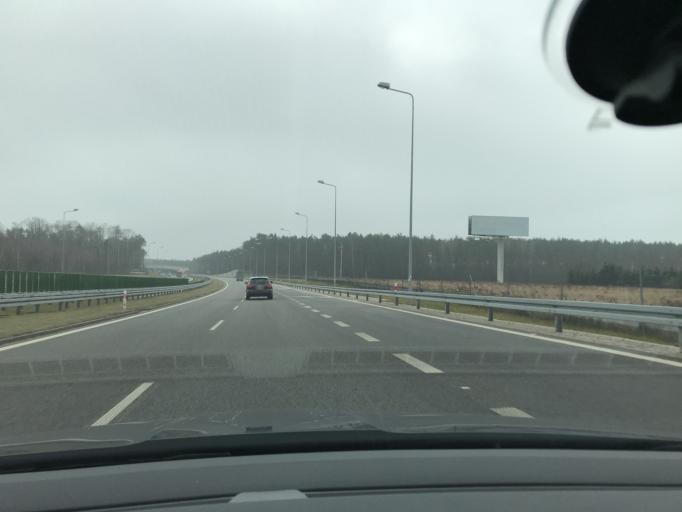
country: PL
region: Lodz Voivodeship
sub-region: Powiat pabianicki
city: Dobron
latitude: 51.6349
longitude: 19.2709
